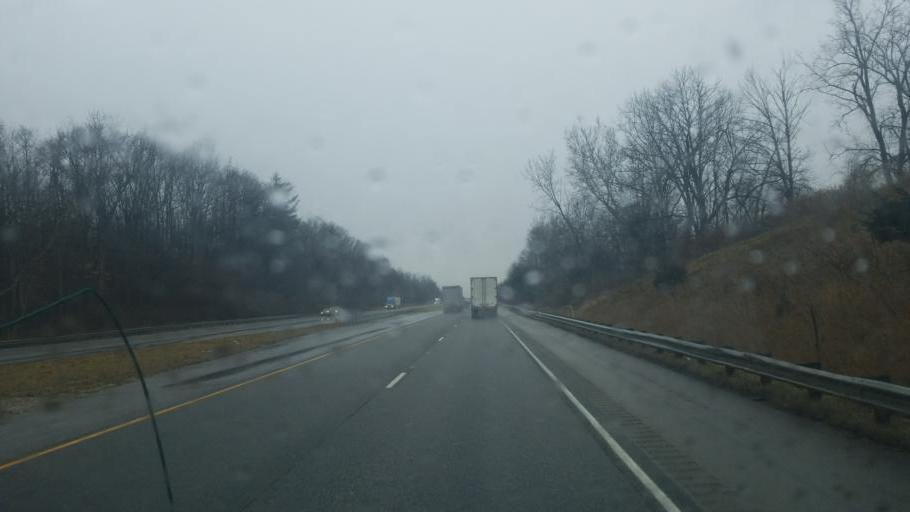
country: US
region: Ohio
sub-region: Preble County
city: New Paris
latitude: 39.8504
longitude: -84.8348
